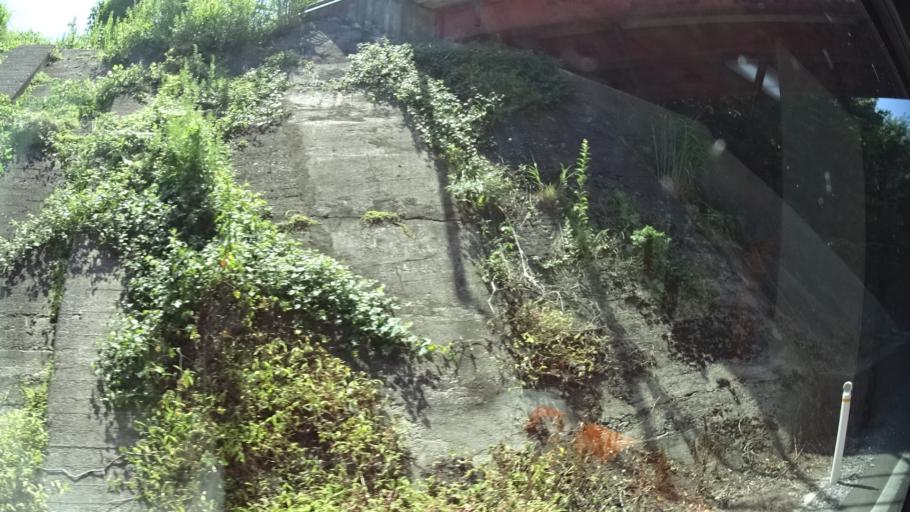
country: JP
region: Iwate
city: Ofunato
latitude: 39.0042
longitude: 141.7131
